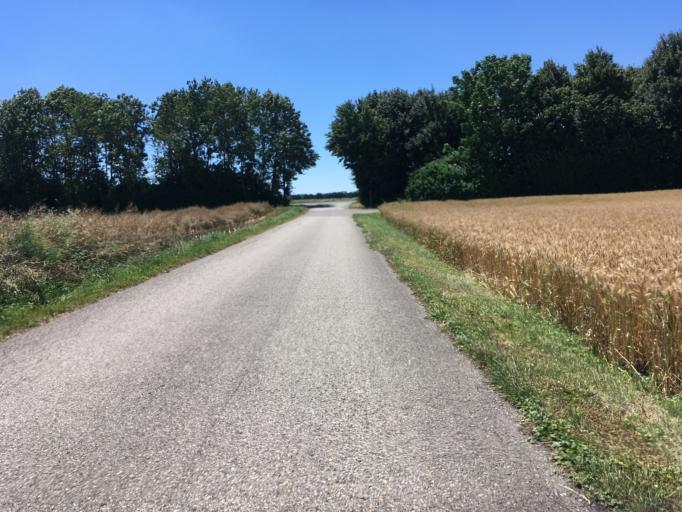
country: CH
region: Vaud
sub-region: Broye-Vully District
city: Avenches
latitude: 46.8932
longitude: 7.0410
